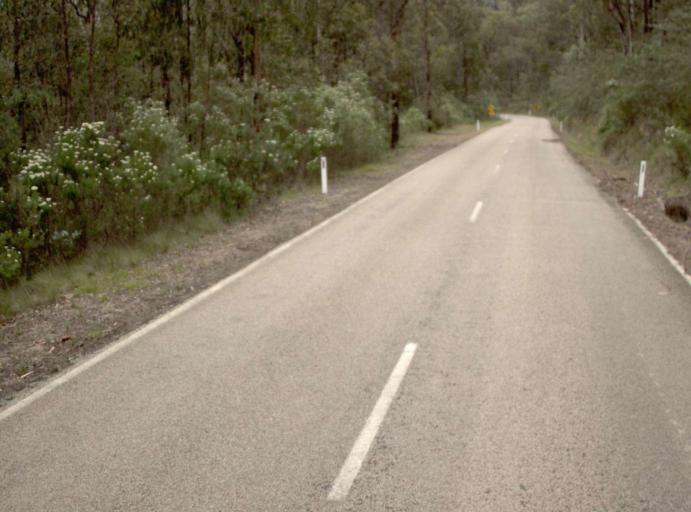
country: AU
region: Victoria
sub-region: East Gippsland
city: Bairnsdale
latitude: -37.6137
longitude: 147.1898
